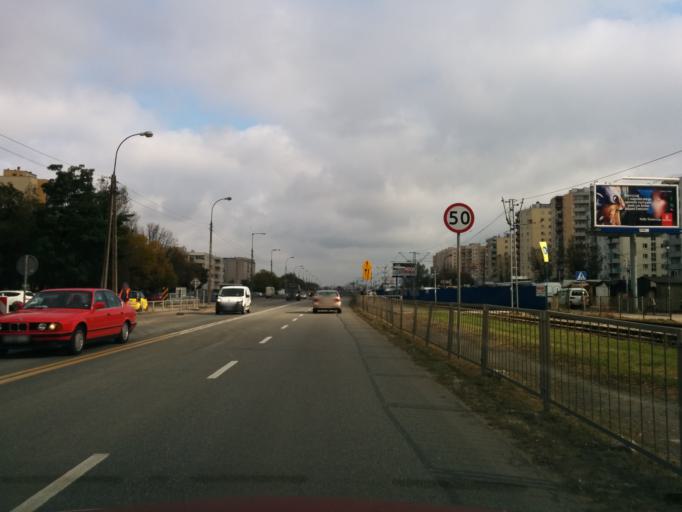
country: PL
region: Masovian Voivodeship
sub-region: Warszawa
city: Bemowo
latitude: 52.2544
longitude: 20.9164
